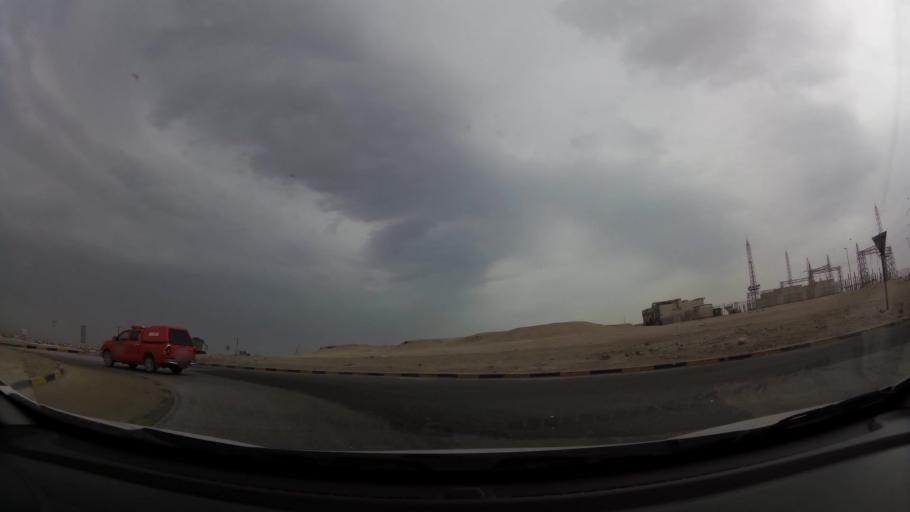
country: BH
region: Central Governorate
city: Dar Kulayb
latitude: 26.0738
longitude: 50.5517
